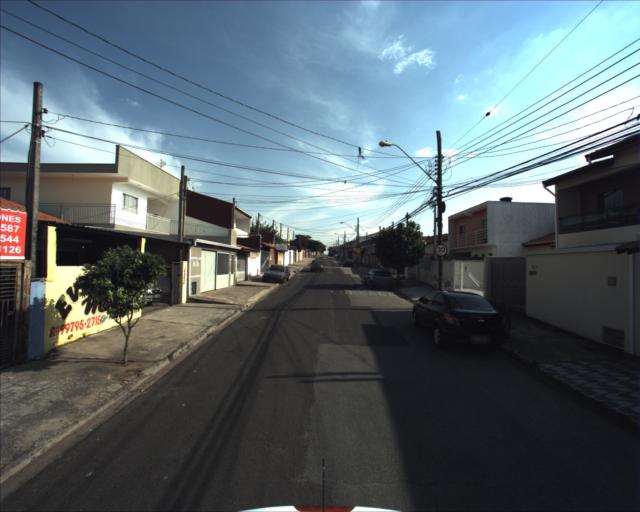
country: BR
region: Sao Paulo
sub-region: Sorocaba
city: Sorocaba
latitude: -23.4959
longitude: -47.5227
